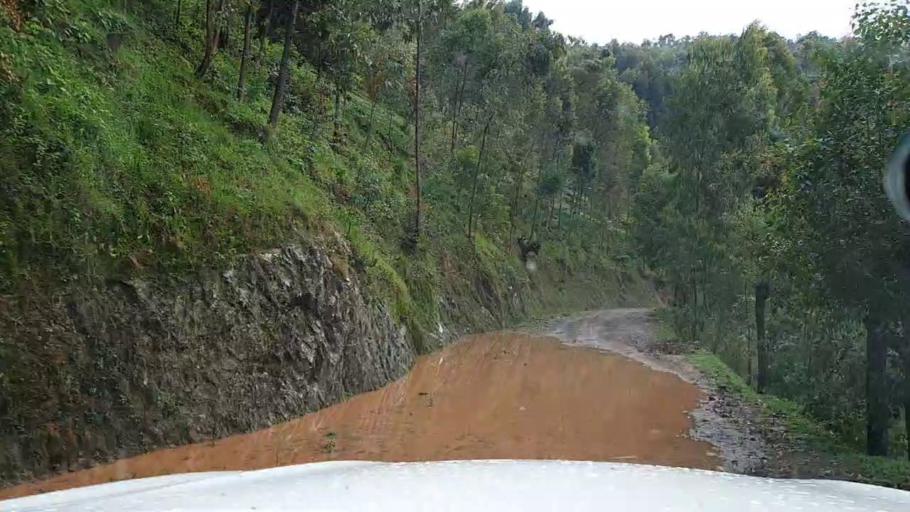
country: RW
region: Northern Province
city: Byumba
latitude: -1.7210
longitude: 29.9044
